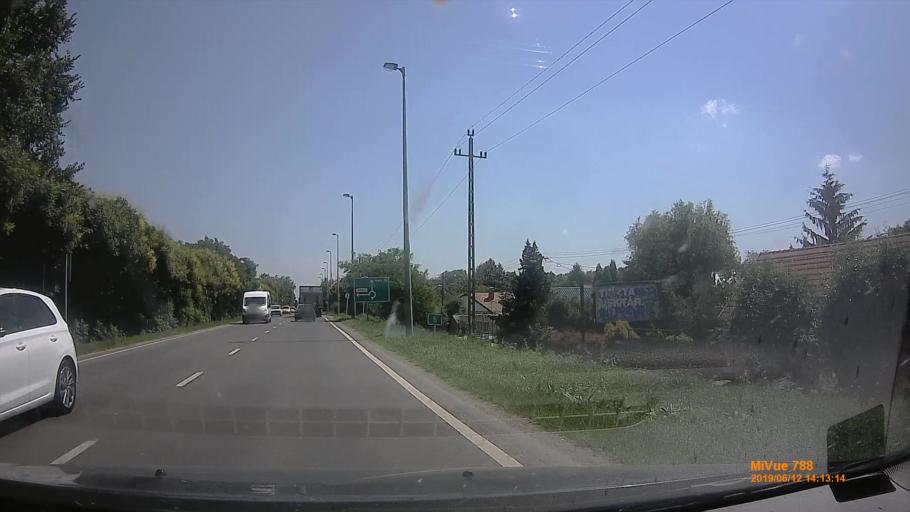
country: HU
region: Csongrad
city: Szeged
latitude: 46.2340
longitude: 20.1729
